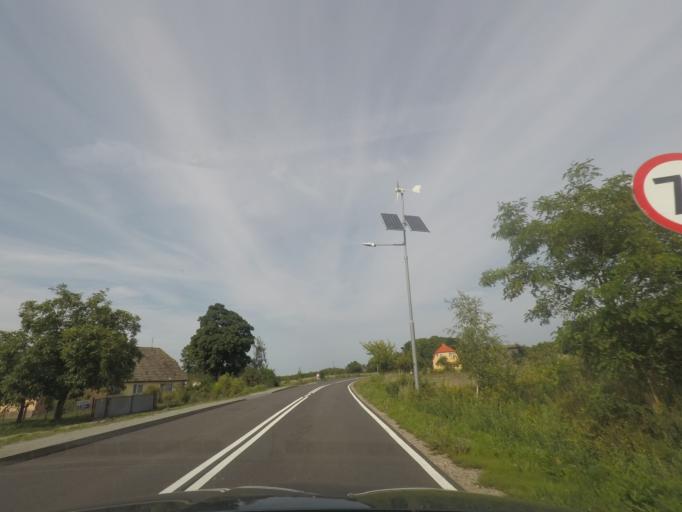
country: PL
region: Pomeranian Voivodeship
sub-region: Powiat slupski
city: Smoldzino
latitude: 54.6001
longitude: 17.1026
